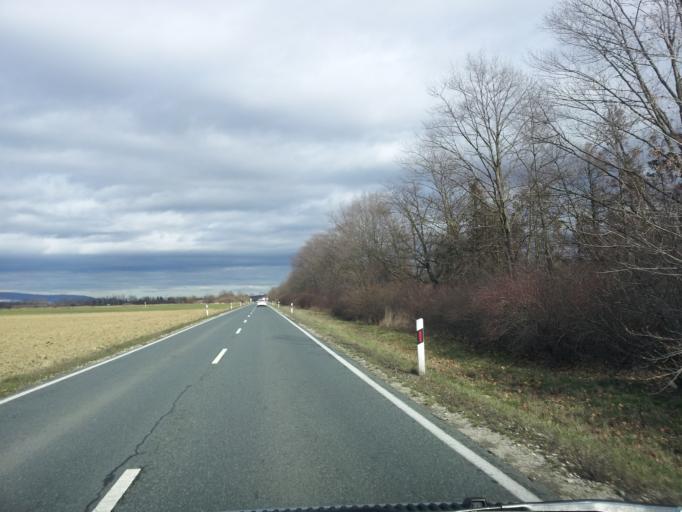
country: HU
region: Vas
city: Gencsapati
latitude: 47.2989
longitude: 16.6062
